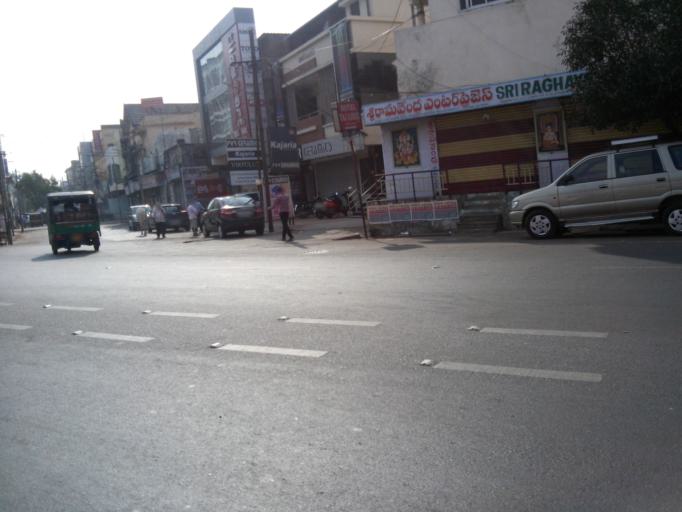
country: IN
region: Andhra Pradesh
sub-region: Krishna
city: Vijayawada
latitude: 16.5127
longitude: 80.6221
